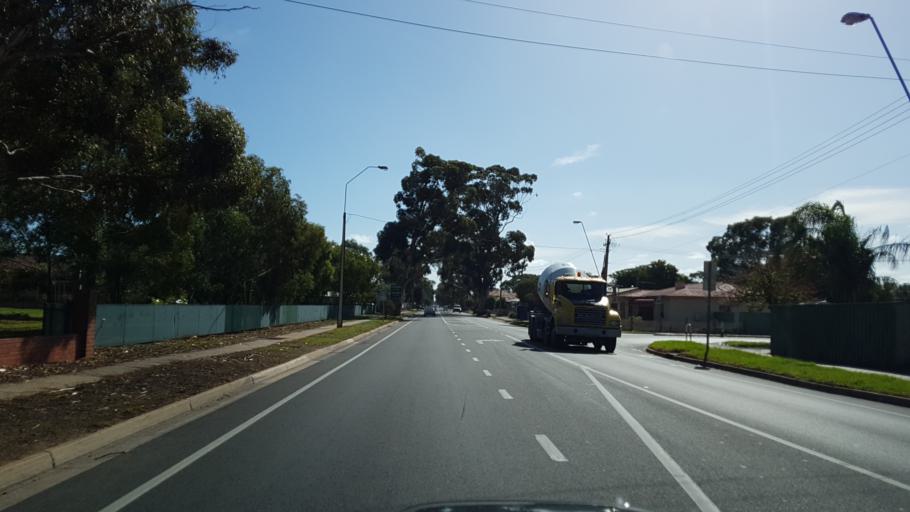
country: AU
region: South Australia
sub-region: Salisbury
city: Salisbury
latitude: -34.7576
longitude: 138.6337
